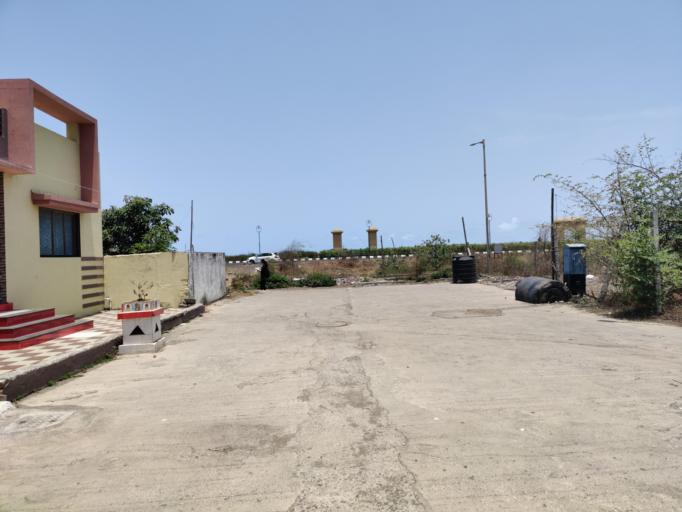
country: IN
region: Daman and Diu
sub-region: Daman District
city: Daman
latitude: 20.4058
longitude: 72.8289
